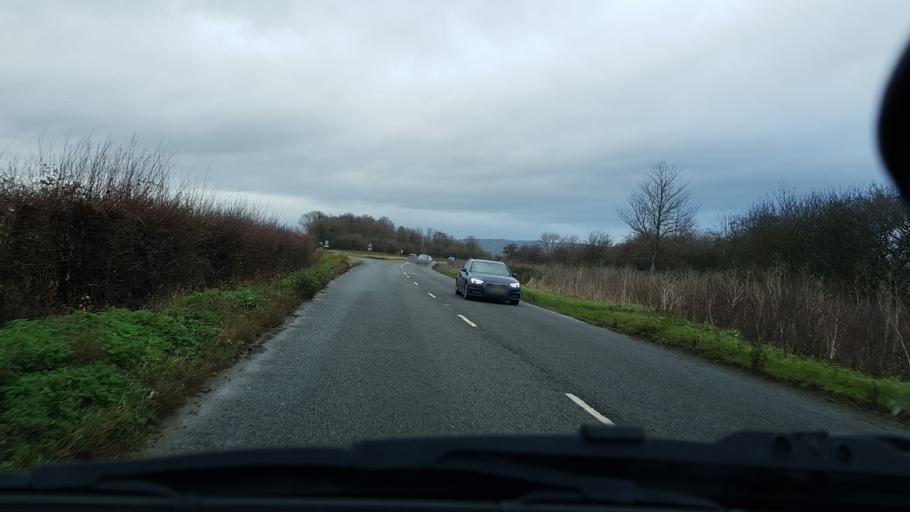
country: GB
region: England
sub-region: Gloucestershire
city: Gotherington
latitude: 51.9828
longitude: -2.0721
